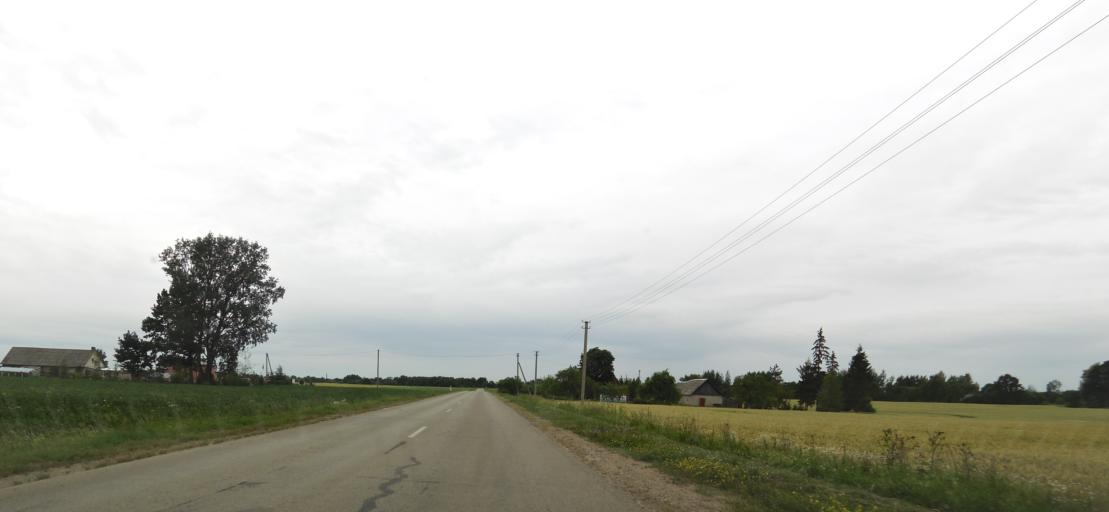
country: LT
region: Panevezys
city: Pasvalys
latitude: 56.0879
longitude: 24.4726
